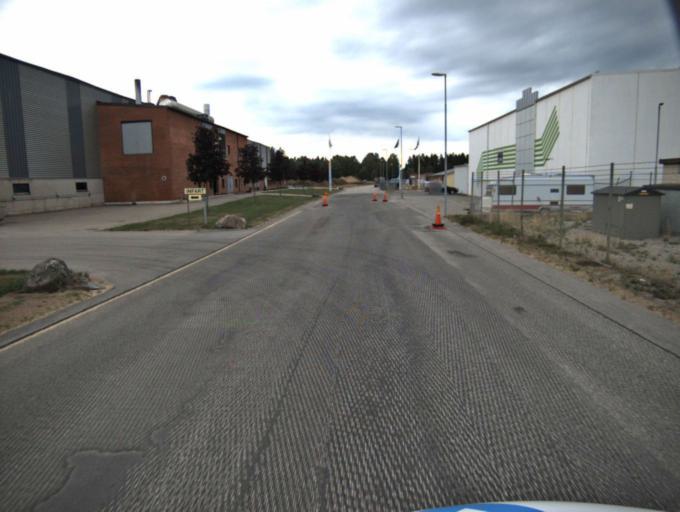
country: SE
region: Vaestra Goetaland
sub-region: Ulricehamns Kommun
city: Ulricehamn
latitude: 57.8264
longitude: 13.4205
